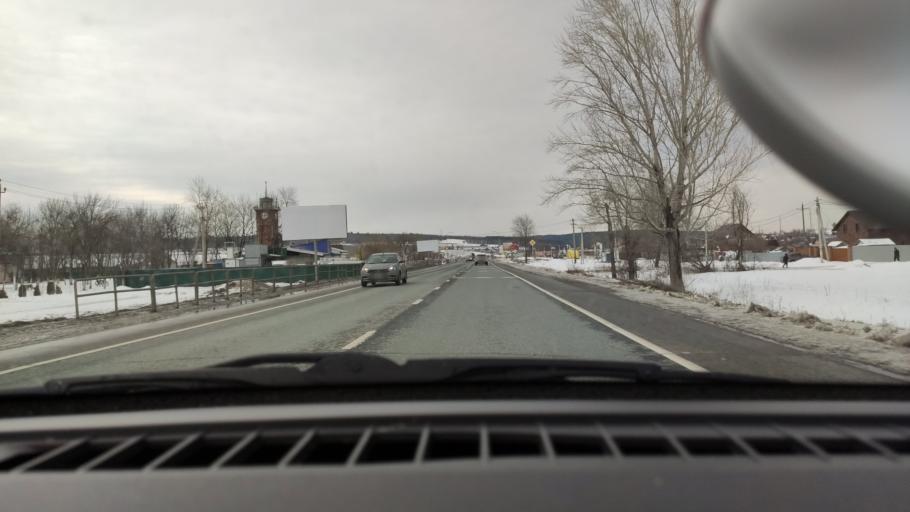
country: RU
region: Samara
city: Kurumoch
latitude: 53.4845
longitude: 50.0256
